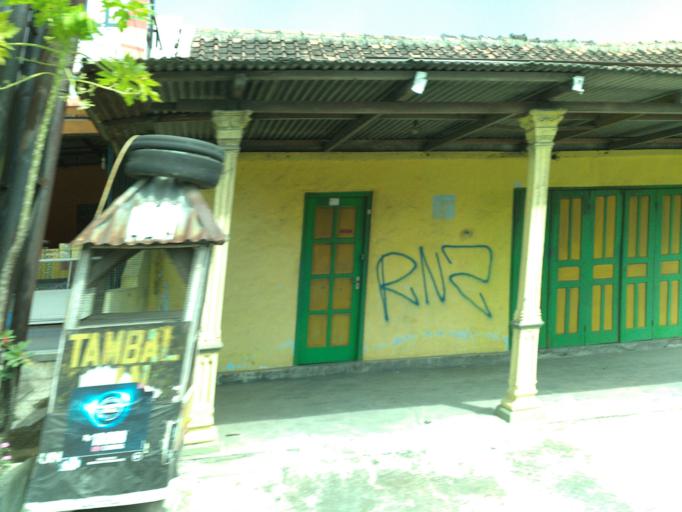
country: ID
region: Central Java
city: Candi Prambanan
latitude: -7.7463
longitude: 110.5255
